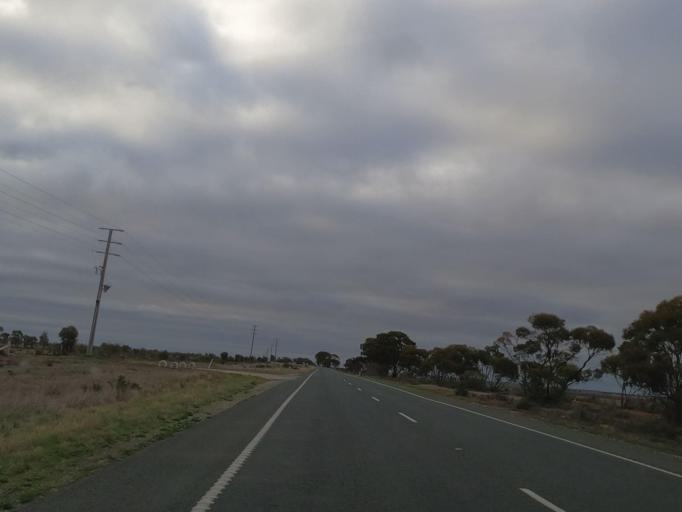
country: AU
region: Victoria
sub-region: Swan Hill
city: Swan Hill
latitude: -35.5785
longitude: 143.7887
